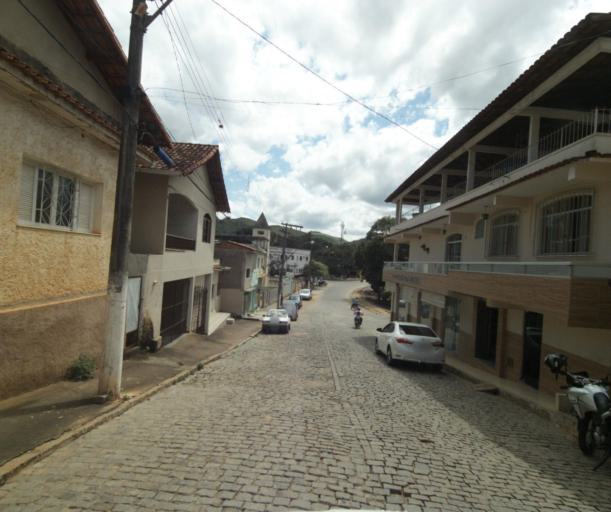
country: BR
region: Espirito Santo
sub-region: Mimoso Do Sul
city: Mimoso do Sul
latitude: -21.0656
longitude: -41.3622
